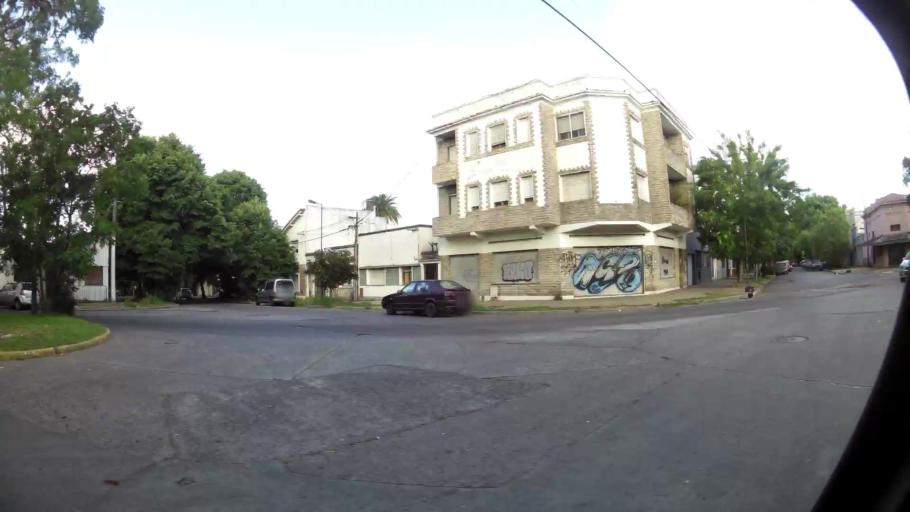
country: AR
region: Buenos Aires
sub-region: Partido de La Plata
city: La Plata
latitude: -34.8964
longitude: -57.9562
